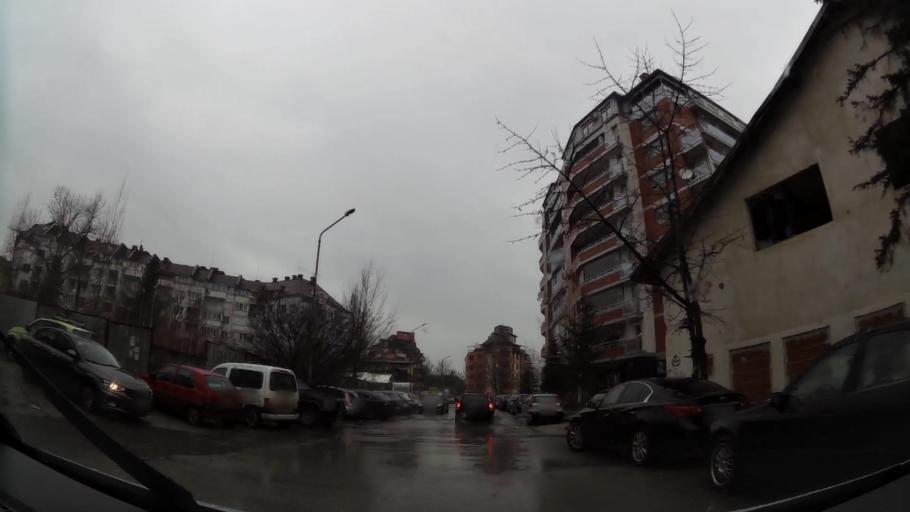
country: BG
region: Sofia-Capital
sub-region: Stolichna Obshtina
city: Sofia
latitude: 42.6438
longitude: 23.3372
